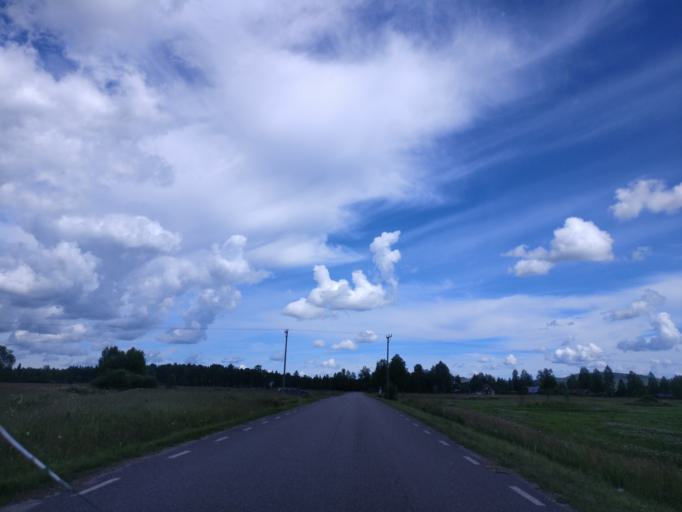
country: SE
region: Vaermland
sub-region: Hagfors Kommun
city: Ekshaerad
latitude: 60.1262
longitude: 13.4559
